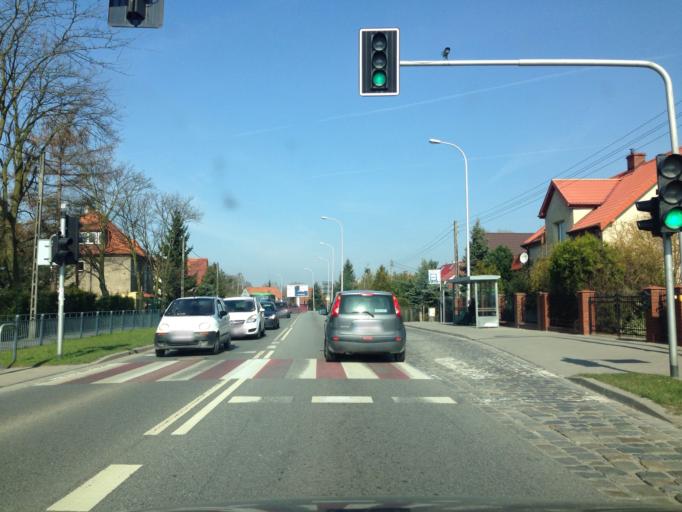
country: PL
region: Lower Silesian Voivodeship
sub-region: Powiat wroclawski
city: Wilczyce
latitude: 51.1031
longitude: 17.1552
